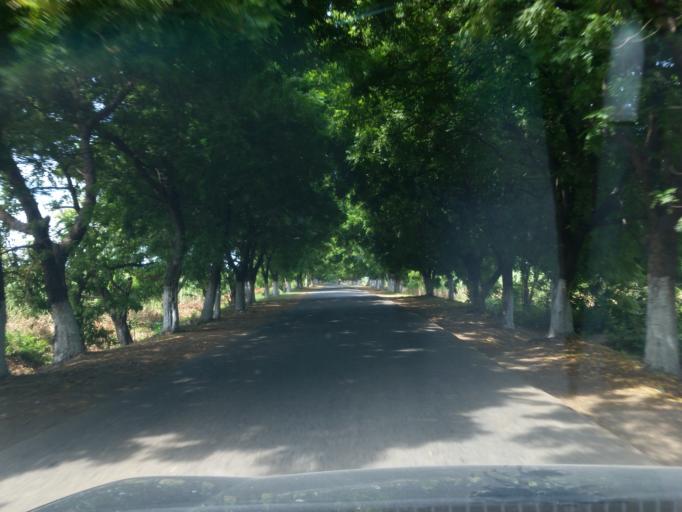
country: NI
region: Managua
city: Masachapa
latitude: 11.8054
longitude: -86.4959
